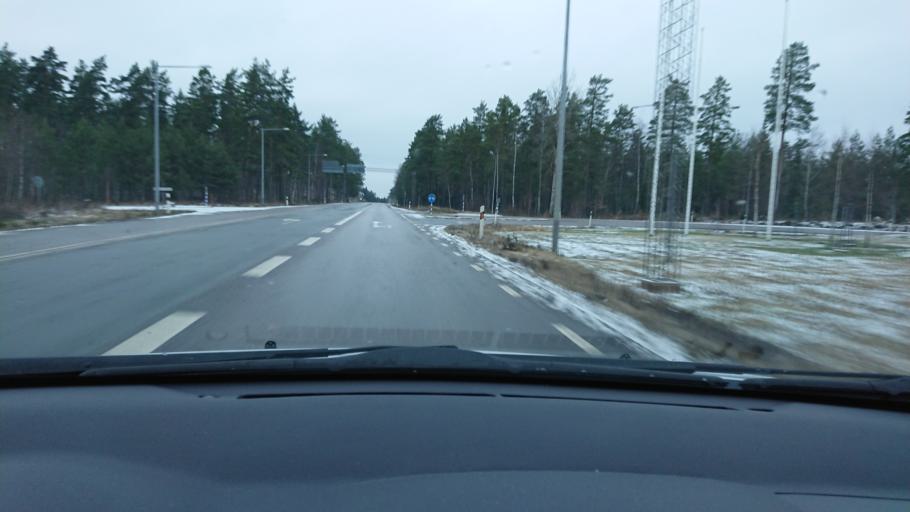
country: SE
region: Kalmar
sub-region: Hultsfreds Kommun
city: Hultsfred
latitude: 57.4883
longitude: 15.8270
